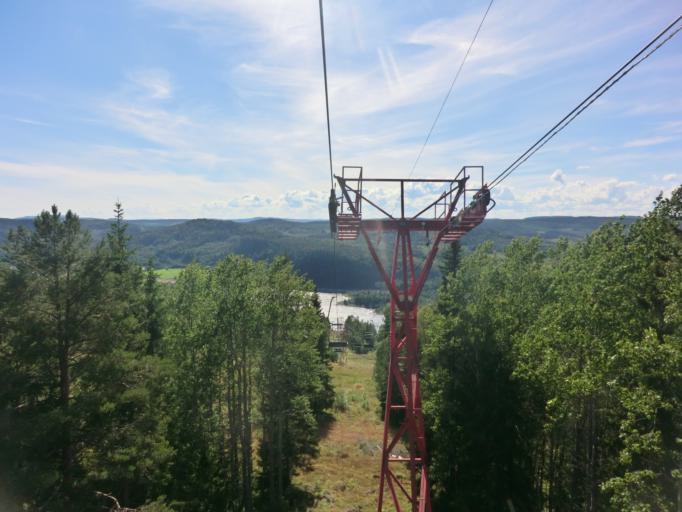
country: SE
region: Vaesternorrland
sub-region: Kramfors Kommun
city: Nordingra
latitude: 63.0747
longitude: 18.3448
